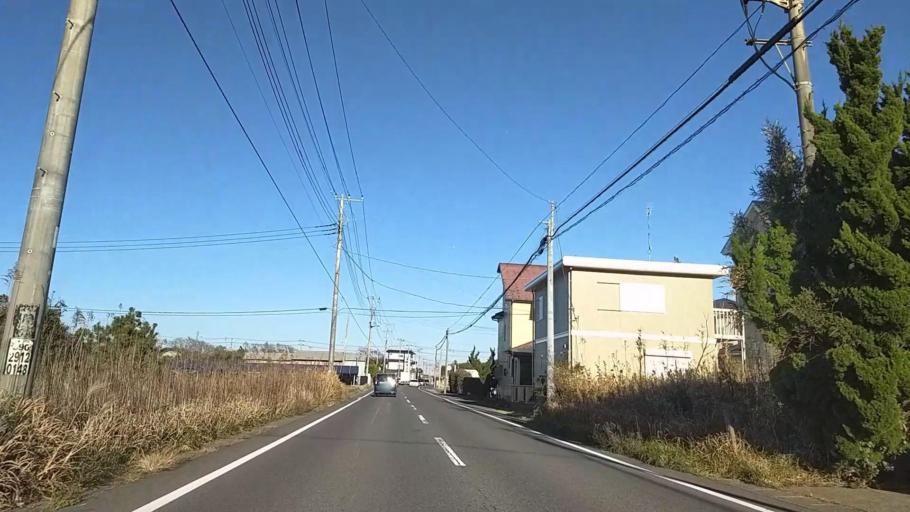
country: JP
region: Chiba
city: Yokaichiba
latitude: 35.6571
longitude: 140.5942
